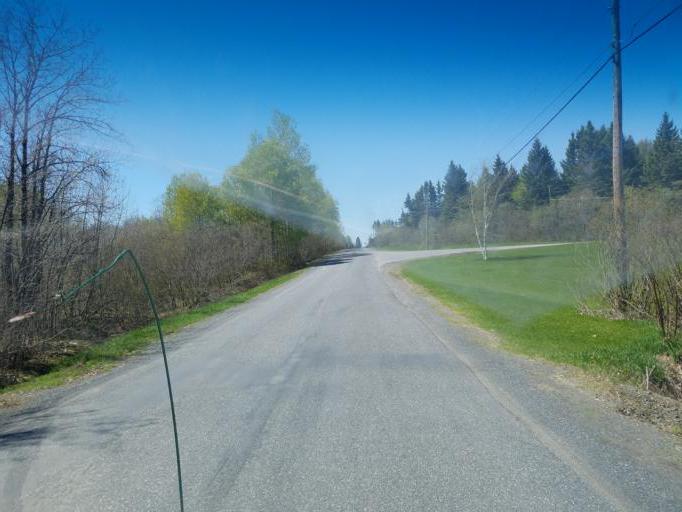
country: US
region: Maine
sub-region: Aroostook County
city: Caribou
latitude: 46.8448
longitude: -68.0443
